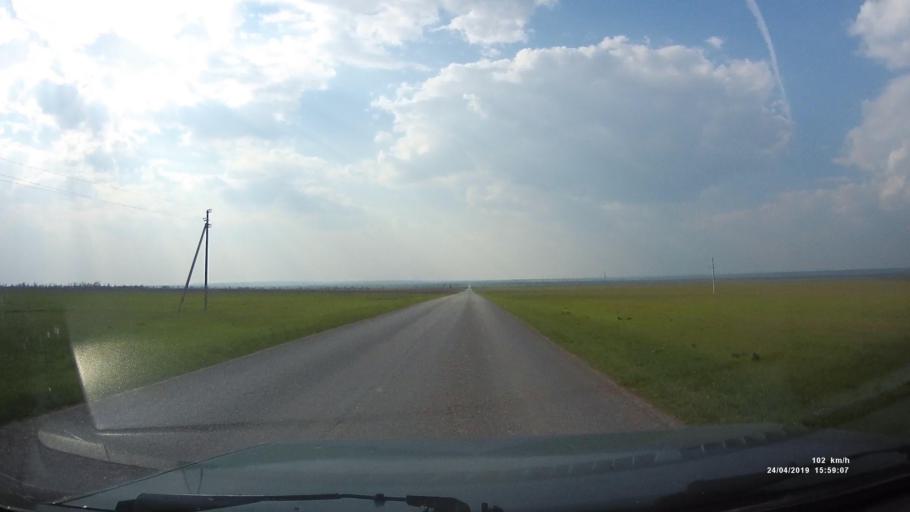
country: RU
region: Kalmykiya
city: Yashalta
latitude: 46.6204
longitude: 42.4779
